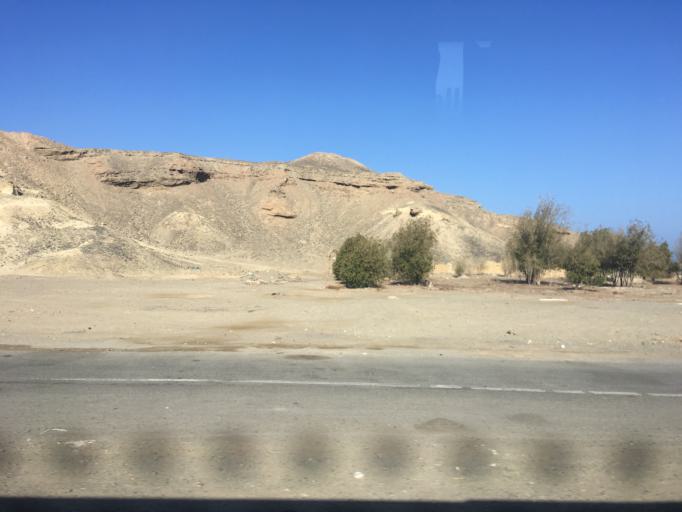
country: EG
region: Red Sea
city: Marsa Alam
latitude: 25.0714
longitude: 34.8886
